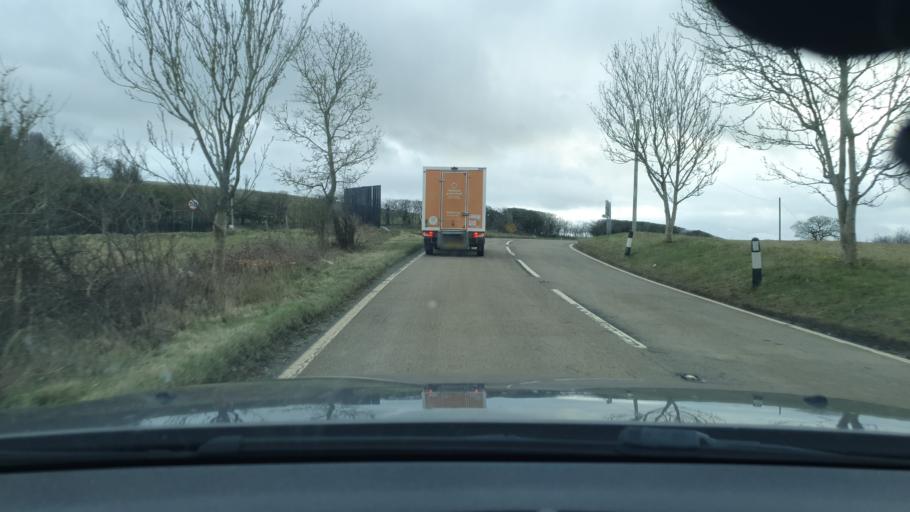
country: GB
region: England
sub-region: West Berkshire
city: Welford
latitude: 51.4994
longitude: -1.4286
